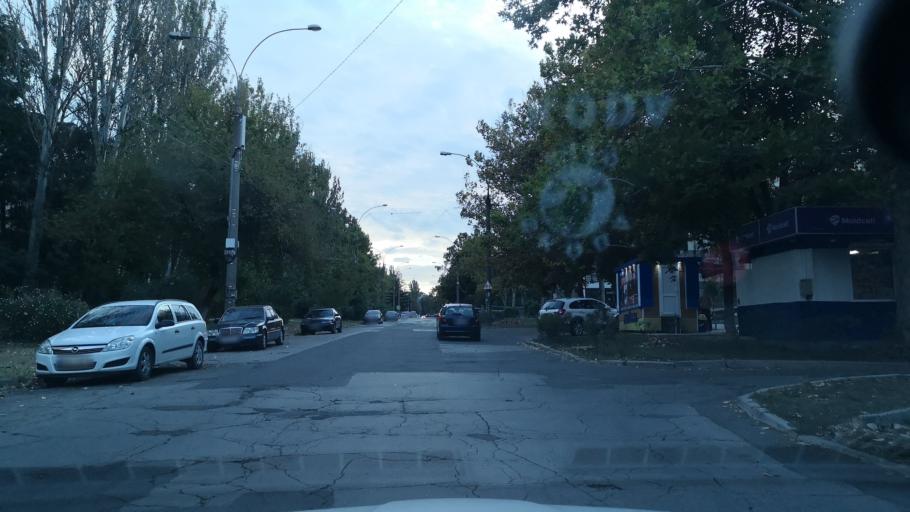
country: MD
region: Chisinau
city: Chisinau
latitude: 46.9877
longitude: 28.8516
